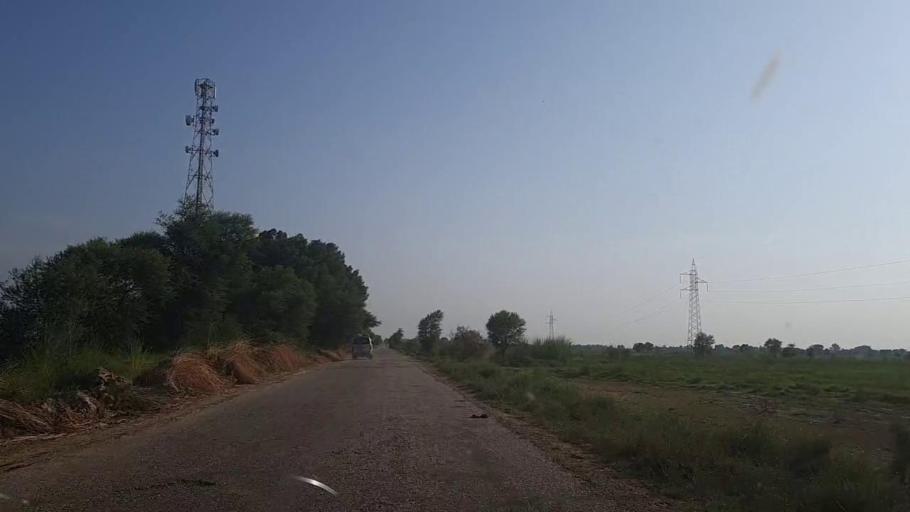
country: PK
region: Sindh
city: Khanpur
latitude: 27.7282
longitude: 69.3036
